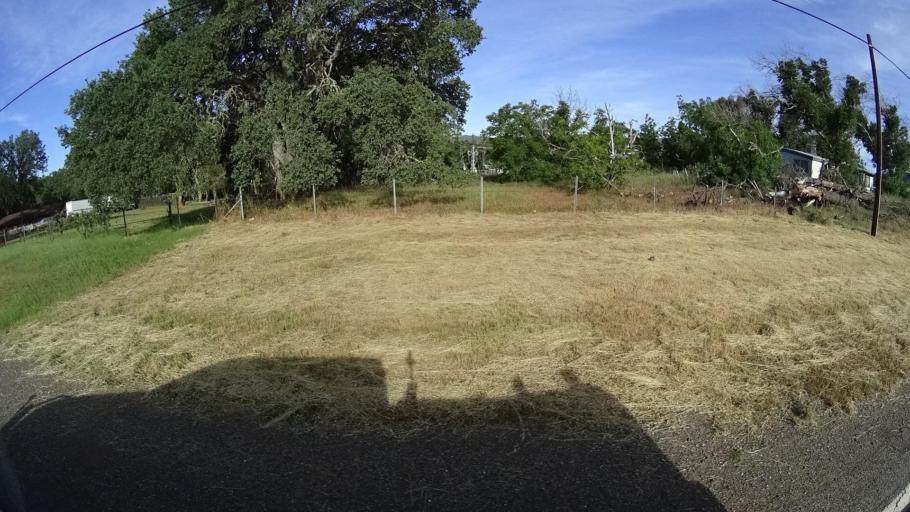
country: US
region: California
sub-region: Lake County
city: North Lakeport
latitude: 39.0770
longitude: -122.9313
